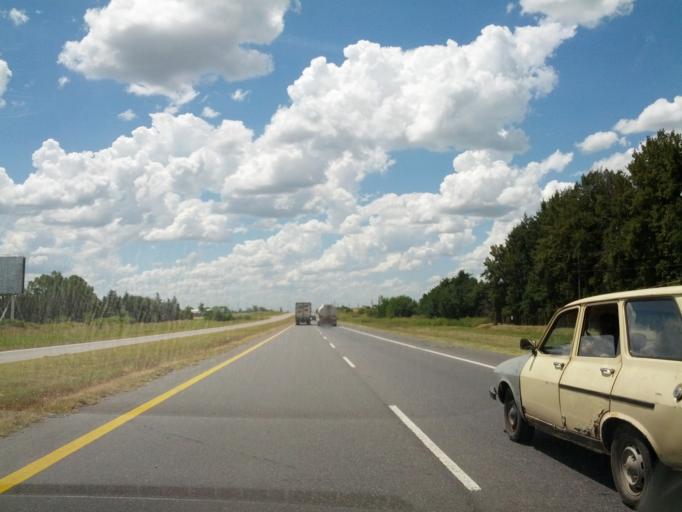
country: AR
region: Entre Rios
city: Gualeguaychu
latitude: -33.0288
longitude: -58.6138
